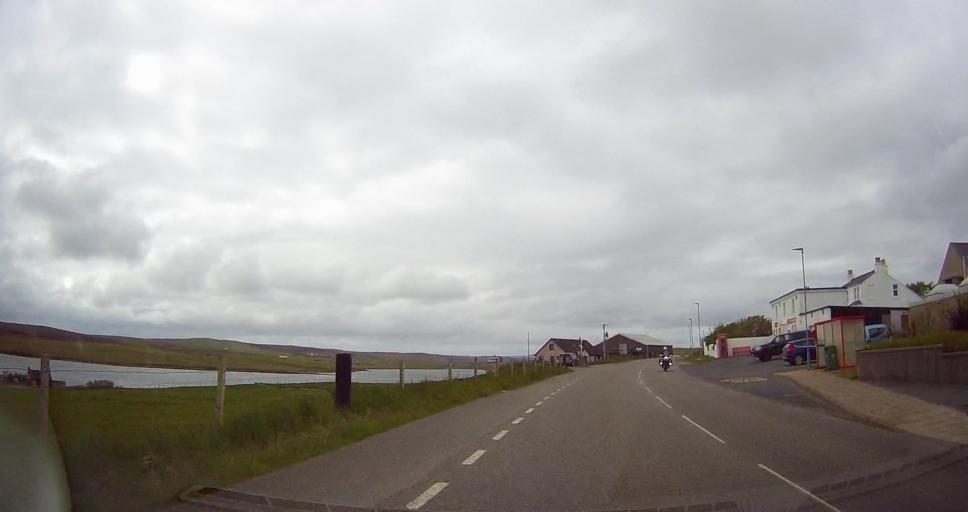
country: GB
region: Scotland
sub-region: Shetland Islands
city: Lerwick
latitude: 60.2529
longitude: -1.4006
